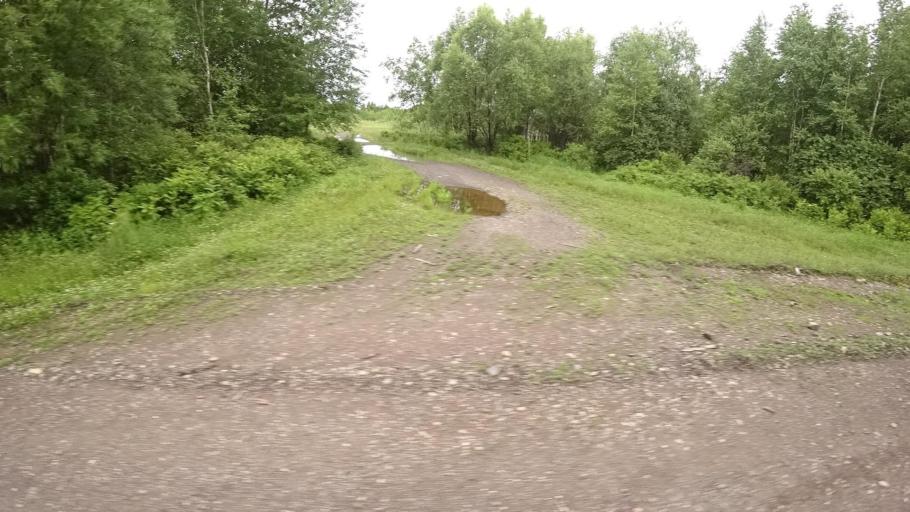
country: RU
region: Khabarovsk Krai
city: Amursk
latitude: 49.9122
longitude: 136.1581
